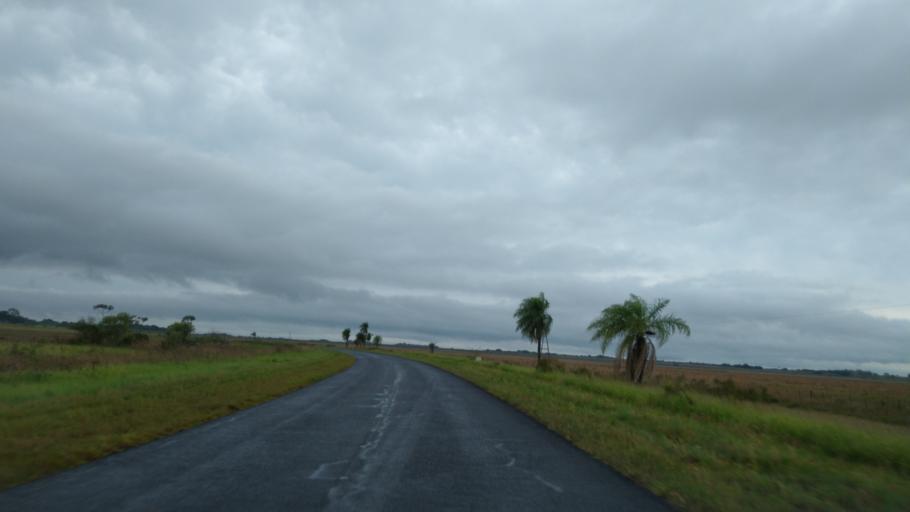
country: AR
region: Corrientes
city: Loreto
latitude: -27.7213
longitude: -57.2319
